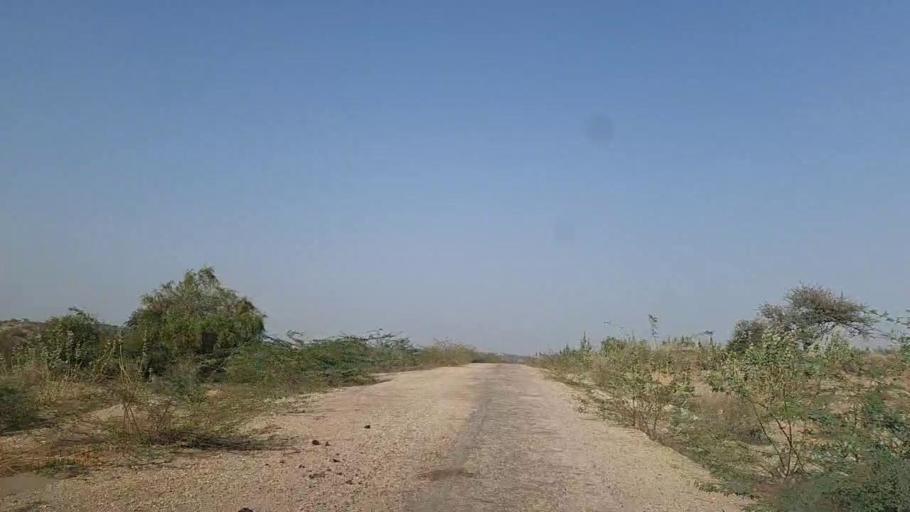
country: PK
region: Sindh
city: Naukot
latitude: 24.6210
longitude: 69.3494
